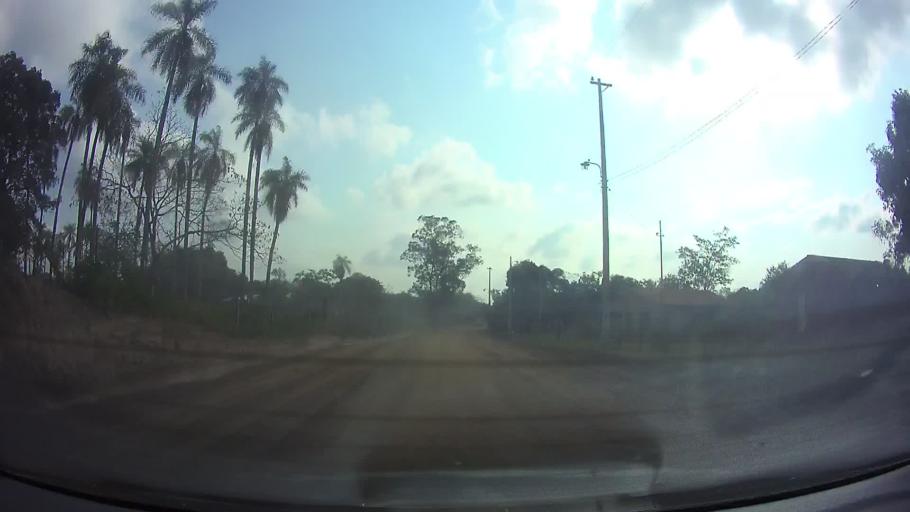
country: PY
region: Cordillera
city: Arroyos y Esteros
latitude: -25.0522
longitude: -57.1792
